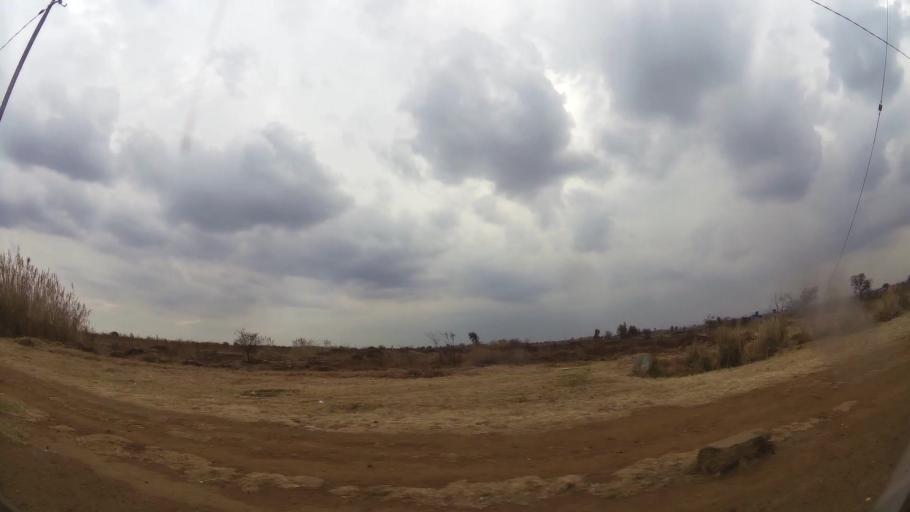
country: ZA
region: Gauteng
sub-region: Ekurhuleni Metropolitan Municipality
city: Germiston
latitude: -26.3818
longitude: 28.1474
